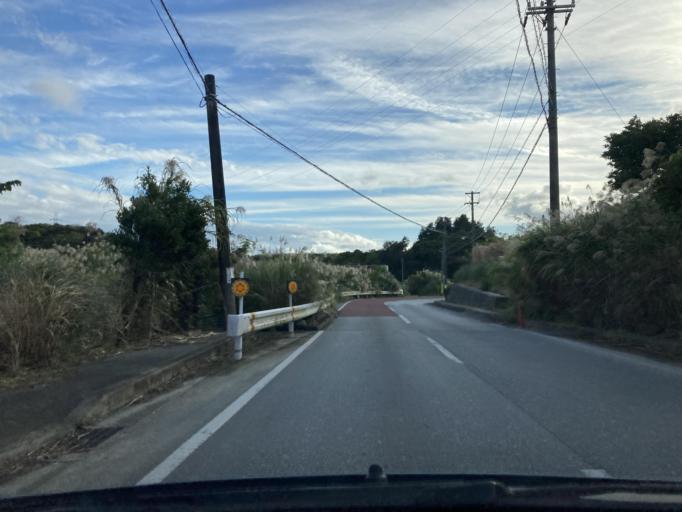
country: JP
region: Okinawa
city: Tomigusuku
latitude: 26.1613
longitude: 127.7387
